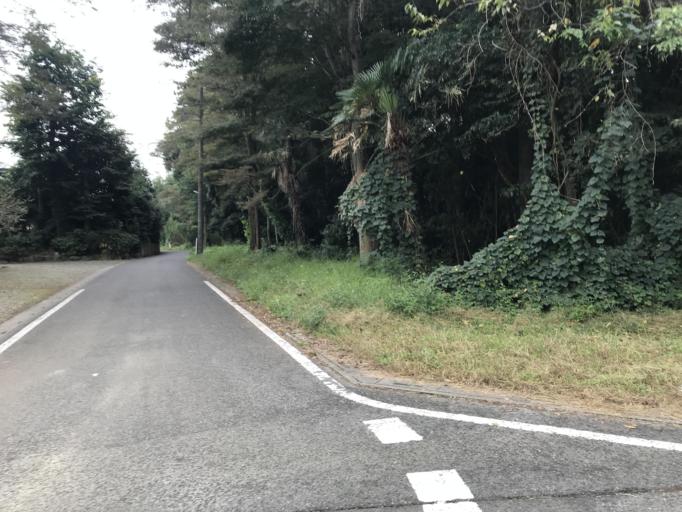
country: JP
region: Saitama
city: Shiraoka
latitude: 36.0044
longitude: 139.6568
